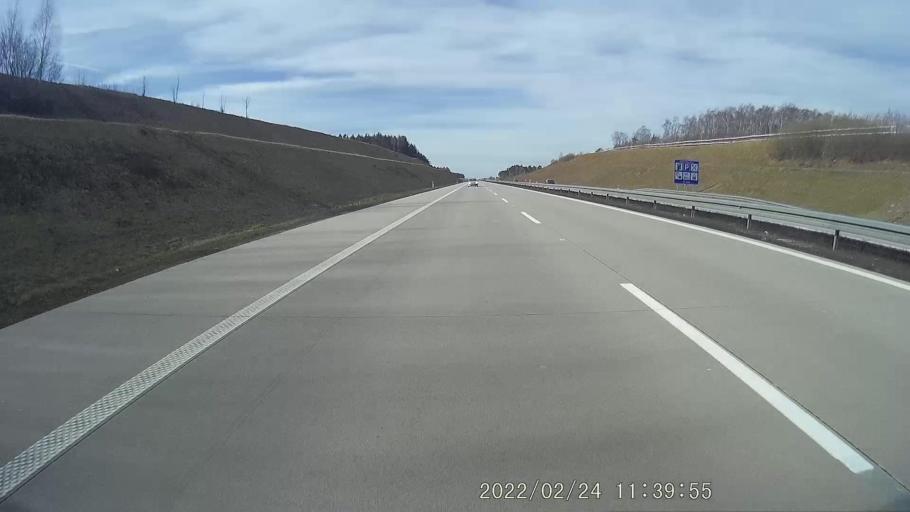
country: PL
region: Lower Silesian Voivodeship
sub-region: Powiat polkowicki
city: Przemkow
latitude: 51.5372
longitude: 15.8672
